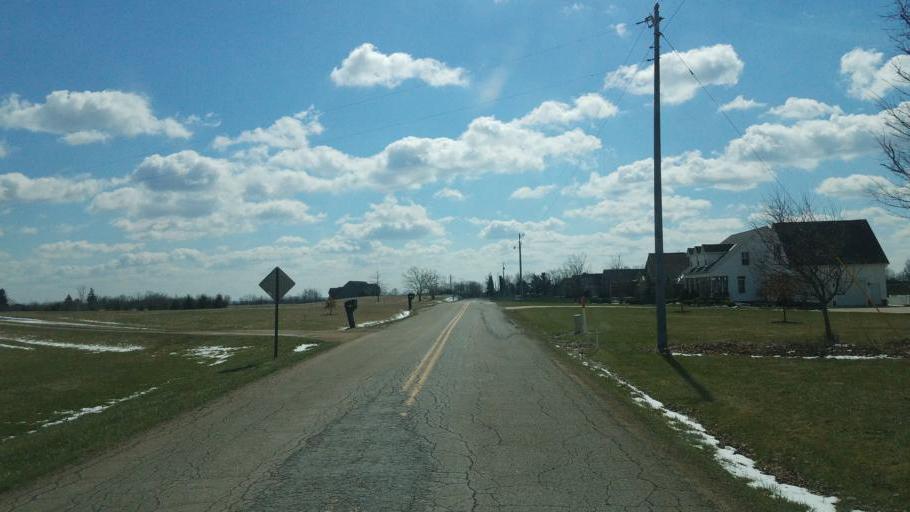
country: US
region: Ohio
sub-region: Knox County
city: Mount Vernon
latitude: 40.3408
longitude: -82.5467
